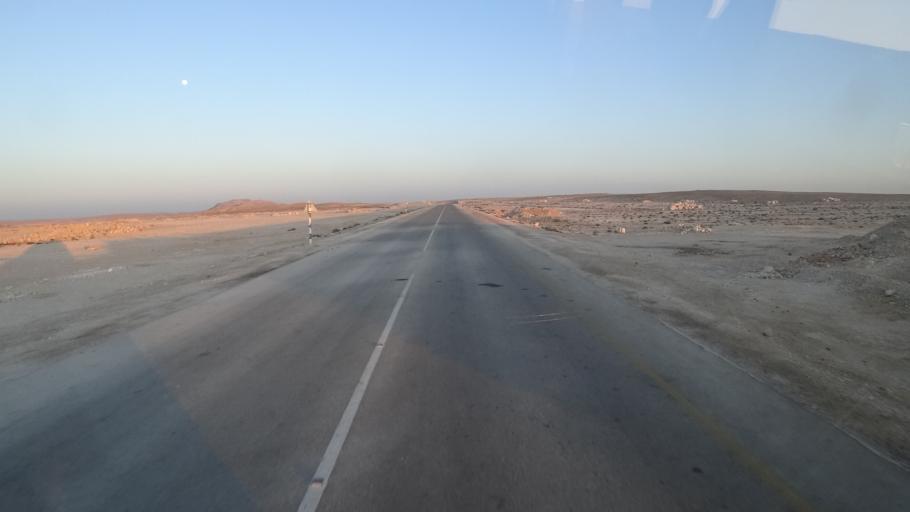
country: YE
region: Al Mahrah
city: Hawf
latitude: 16.9516
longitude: 53.3461
